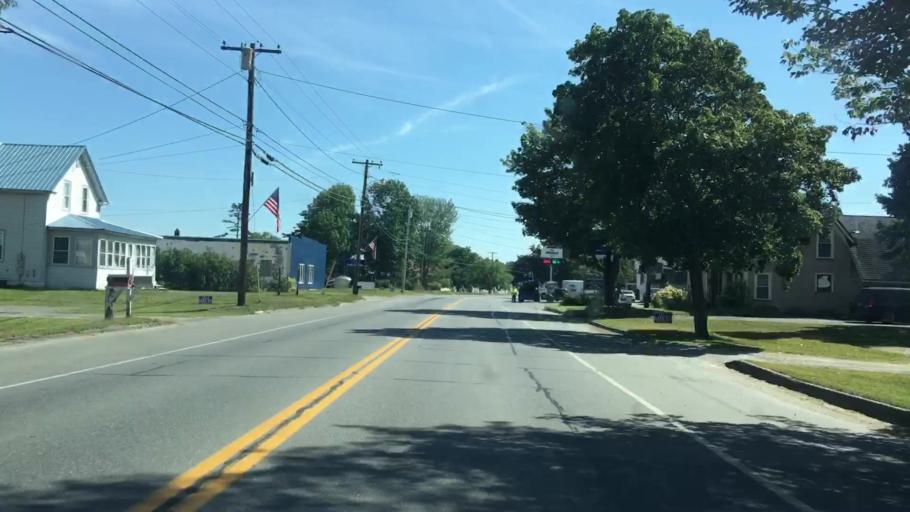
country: US
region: Maine
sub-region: Piscataquis County
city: Milo
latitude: 45.2619
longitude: -68.9894
